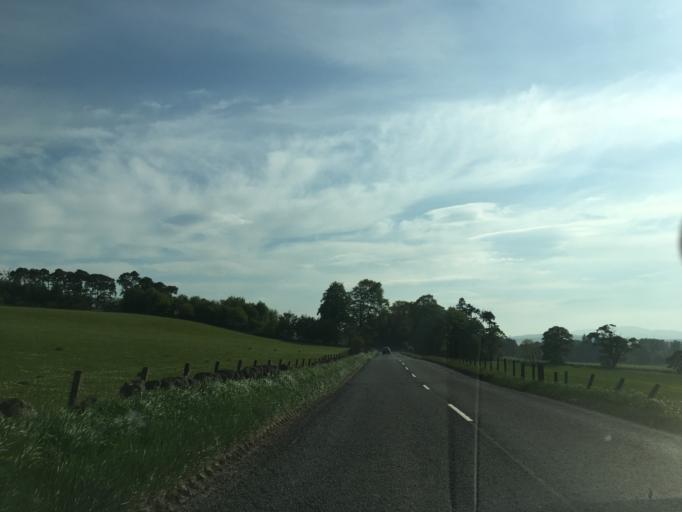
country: GB
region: Scotland
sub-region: The Scottish Borders
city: West Linton
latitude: 55.7367
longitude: -3.3036
